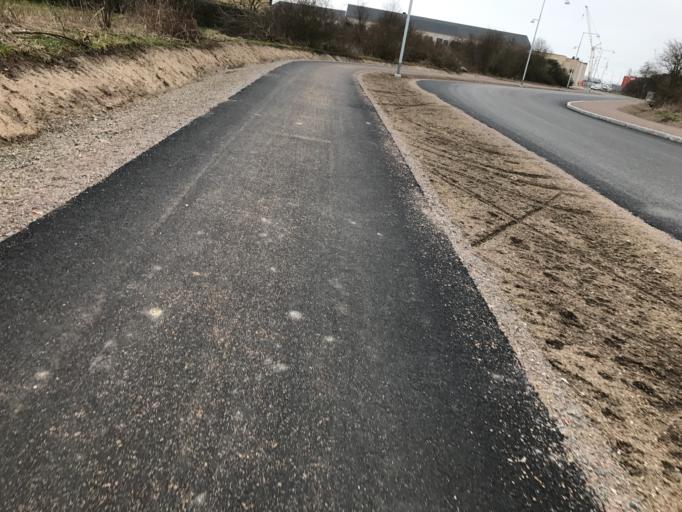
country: SE
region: Skane
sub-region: Landskrona
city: Landskrona
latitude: 55.8997
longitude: 12.8165
